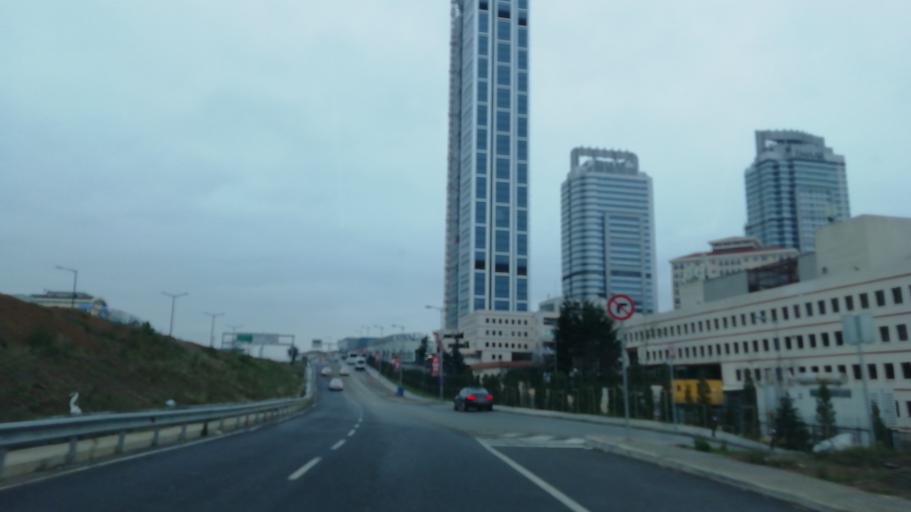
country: TR
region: Istanbul
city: UEskuedar
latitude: 41.0055
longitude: 29.0675
